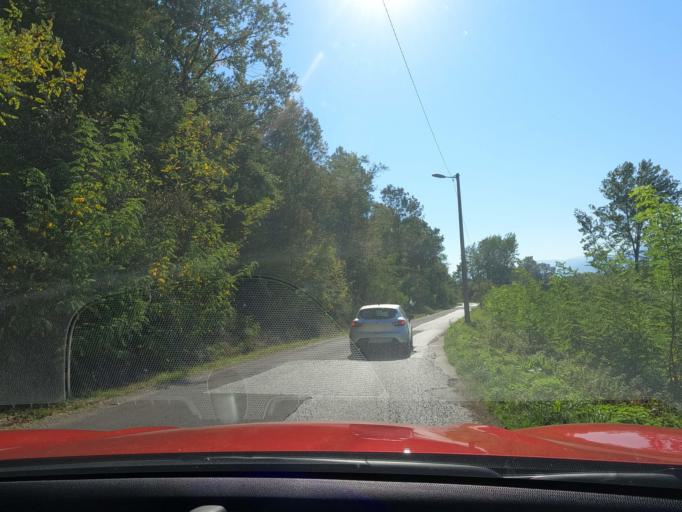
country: RS
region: Central Serbia
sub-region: Raski Okrug
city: Kraljevo
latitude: 43.7352
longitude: 20.7418
